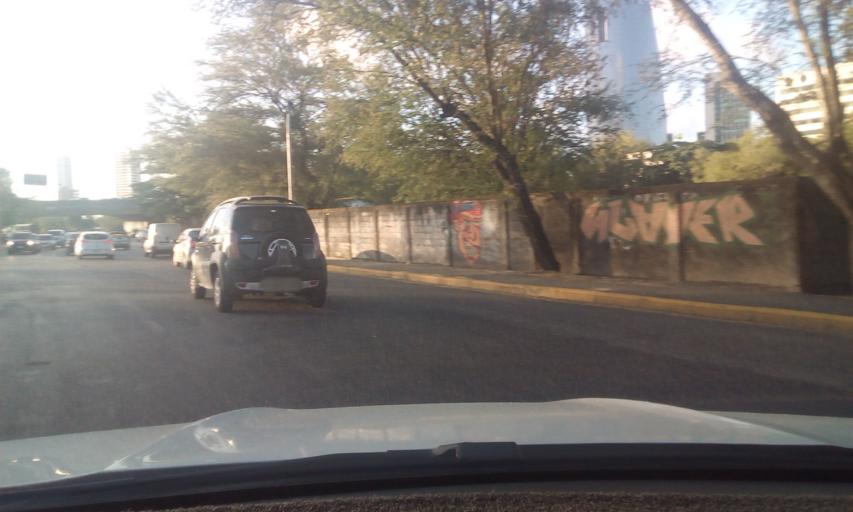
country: BR
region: Pernambuco
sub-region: Recife
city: Recife
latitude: -8.0694
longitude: -34.8953
